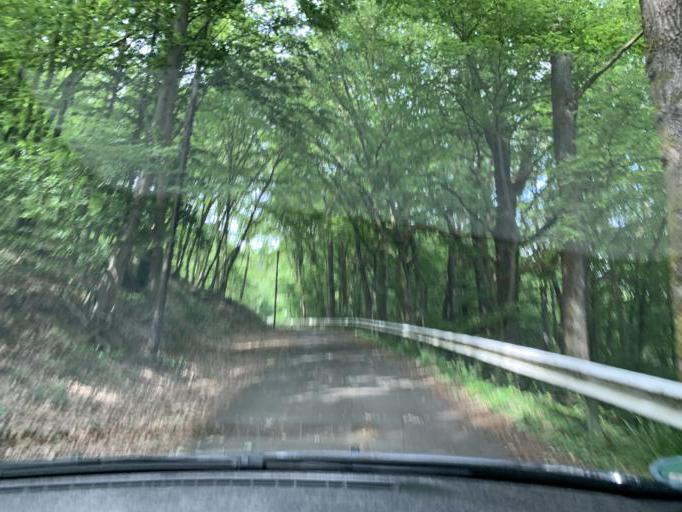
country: DE
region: North Rhine-Westphalia
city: Heimbach
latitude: 50.6475
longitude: 6.4136
